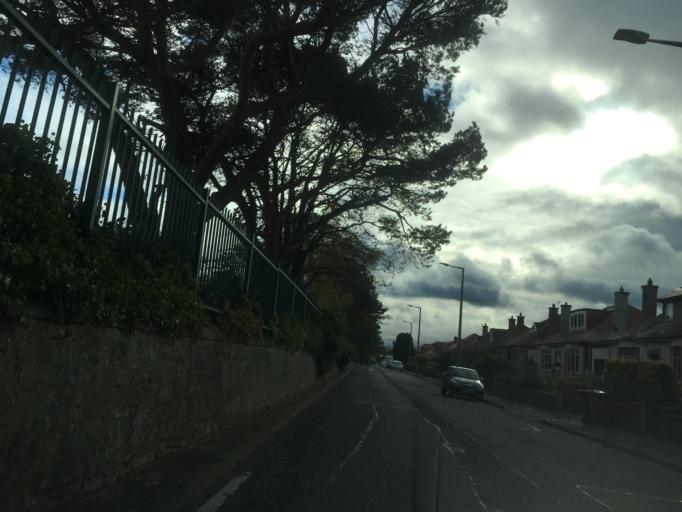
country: GB
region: Scotland
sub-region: Midlothian
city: Loanhead
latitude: 55.9081
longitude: -3.1680
